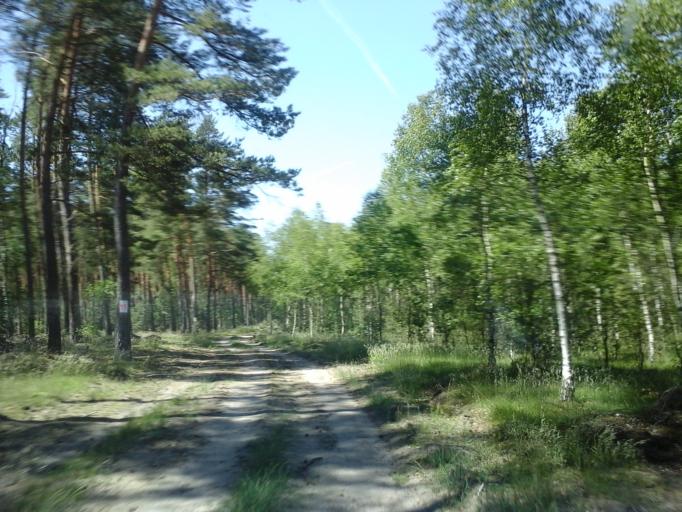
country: PL
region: West Pomeranian Voivodeship
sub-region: Powiat drawski
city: Kalisz Pomorski
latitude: 53.1414
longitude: 15.9085
